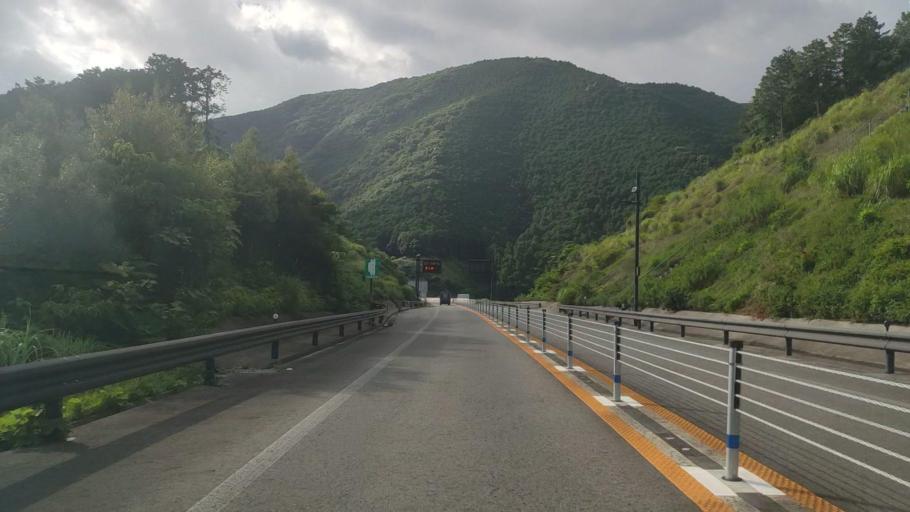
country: JP
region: Wakayama
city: Tanabe
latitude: 33.5595
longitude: 135.5063
